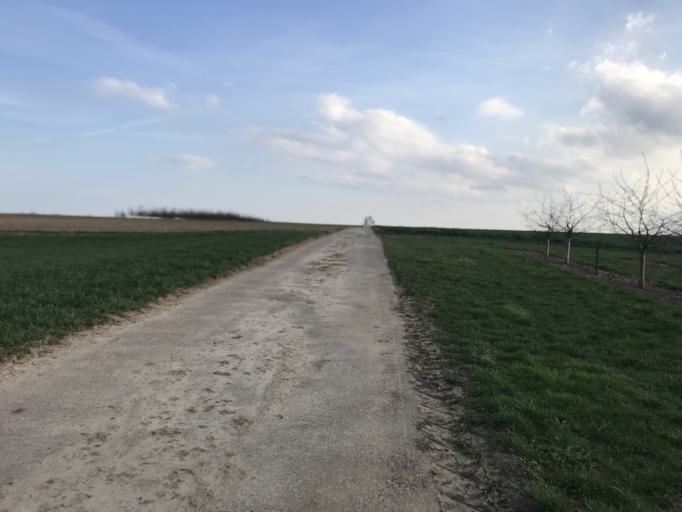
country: DE
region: Rheinland-Pfalz
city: Essenheim
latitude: 49.9432
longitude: 8.1643
